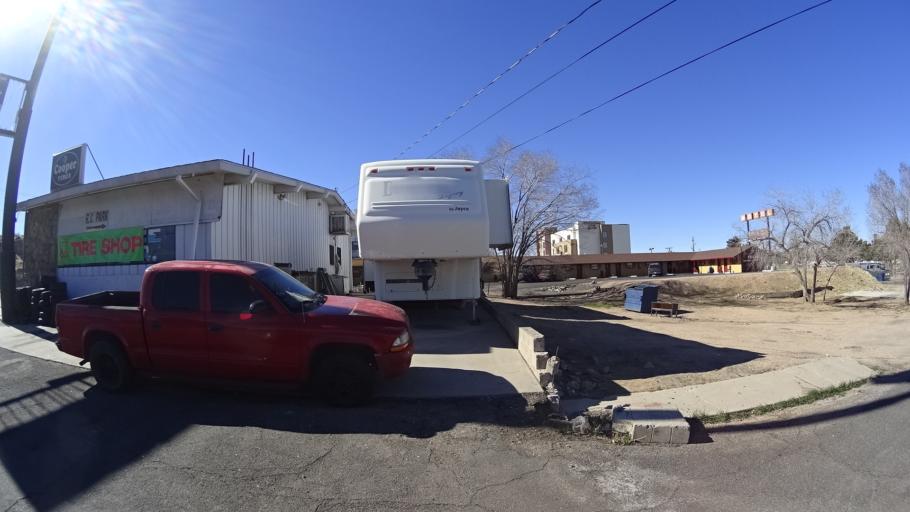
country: US
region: Arizona
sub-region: Mohave County
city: Kingman
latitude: 35.2163
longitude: -114.0125
